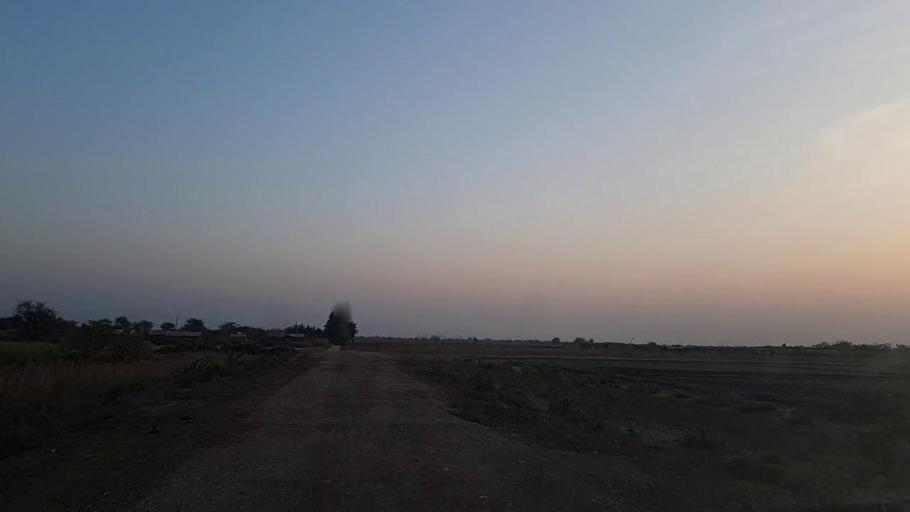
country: PK
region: Sindh
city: Naukot
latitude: 24.9707
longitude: 69.4273
